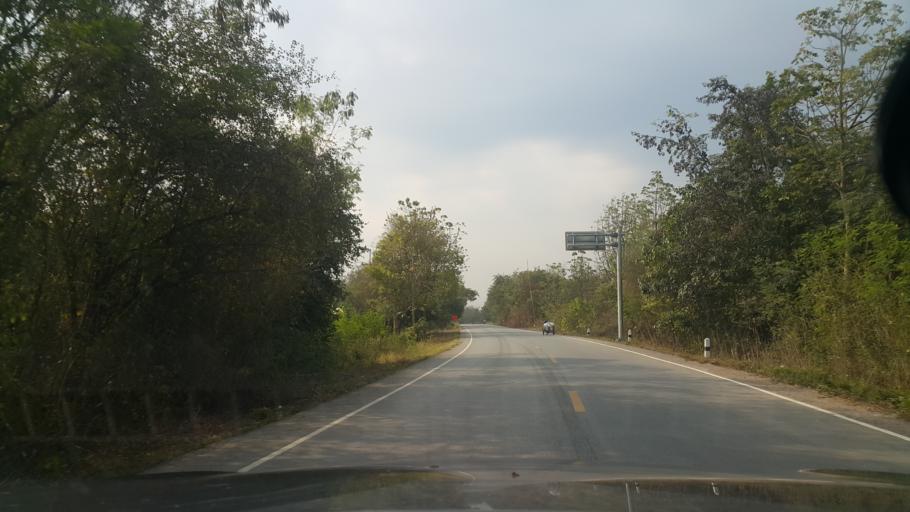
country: TH
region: Sukhothai
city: Thung Saliam
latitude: 17.2260
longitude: 99.5121
